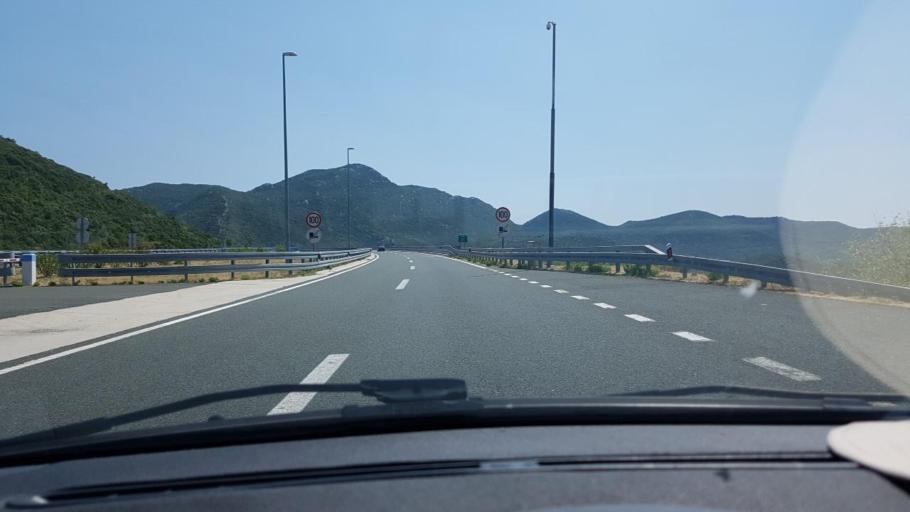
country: HR
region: Dubrovacko-Neretvanska
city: Komin
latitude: 43.1122
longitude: 17.4786
